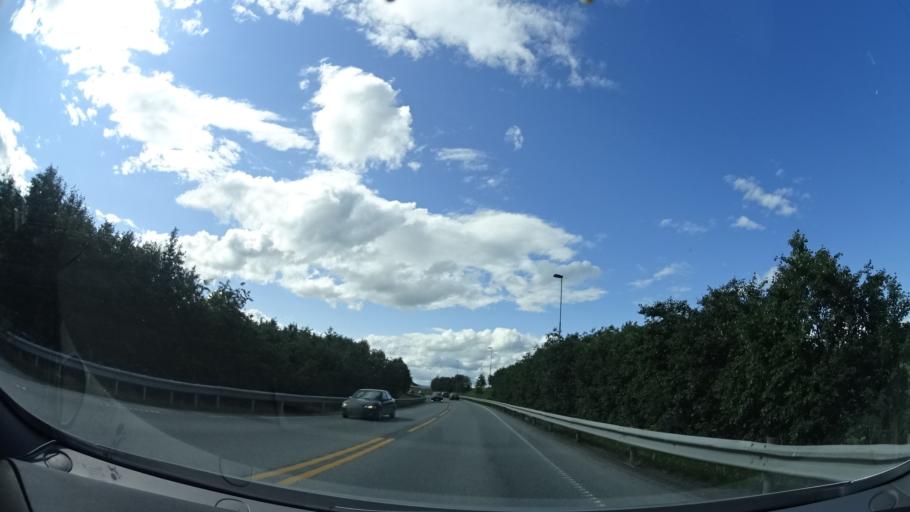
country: NO
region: Sor-Trondelag
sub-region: Melhus
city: Melhus
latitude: 63.3232
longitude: 10.3044
